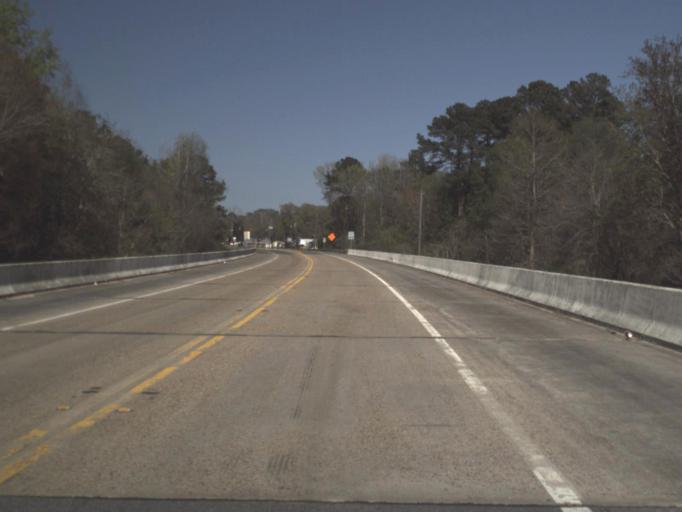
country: US
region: Florida
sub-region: Walton County
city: DeFuniak Springs
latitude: 30.7245
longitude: -85.9407
